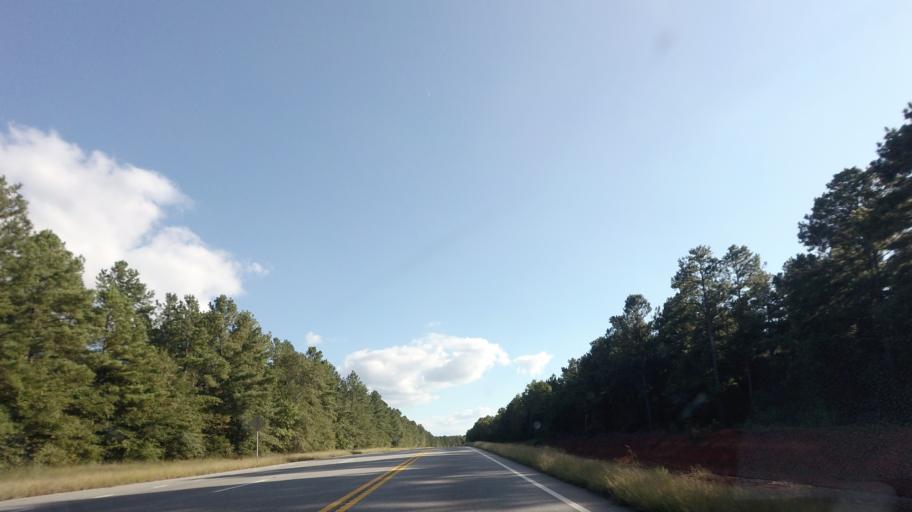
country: US
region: Georgia
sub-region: Lamar County
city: Barnesville
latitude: 32.9869
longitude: -84.2017
